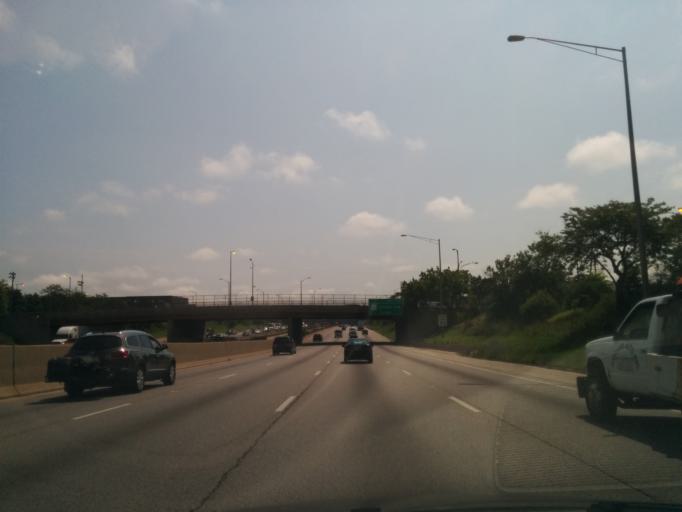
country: US
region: Illinois
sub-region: Cook County
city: Cicero
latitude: 41.8713
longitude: -87.7562
